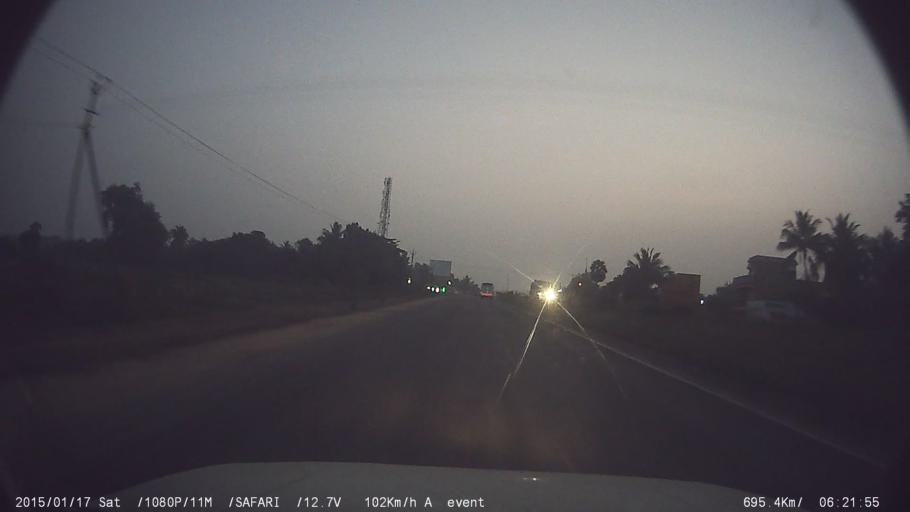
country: IN
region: Tamil Nadu
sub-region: Kancheepuram
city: Wallajahbad
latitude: 12.9080
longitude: 79.8322
